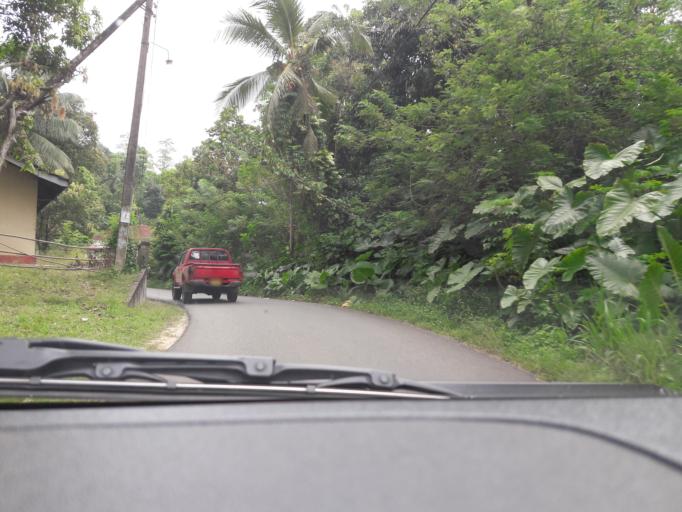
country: LK
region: Southern
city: Galle
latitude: 6.1824
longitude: 80.2988
